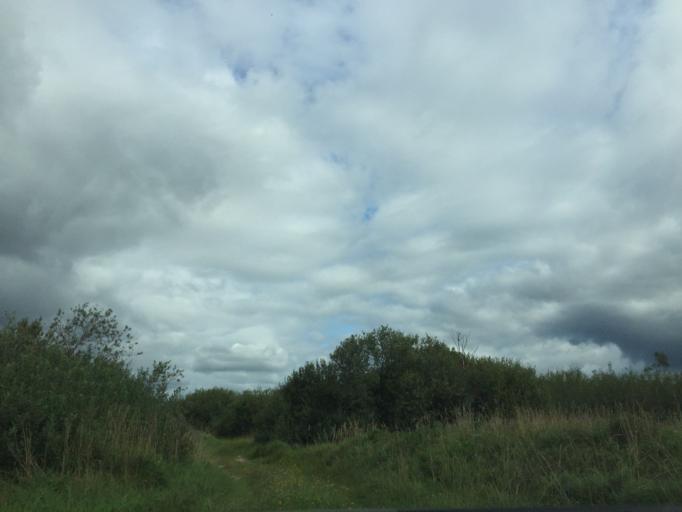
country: LV
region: Pargaujas
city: Stalbe
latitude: 57.4952
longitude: 24.9133
